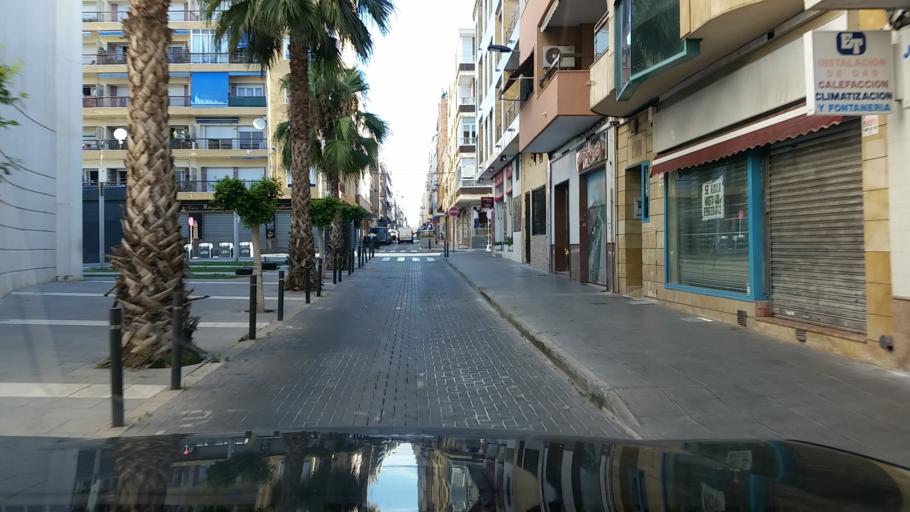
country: ES
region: Valencia
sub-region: Provincia de Alicante
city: Torrevieja
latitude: 37.9764
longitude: -0.6762
